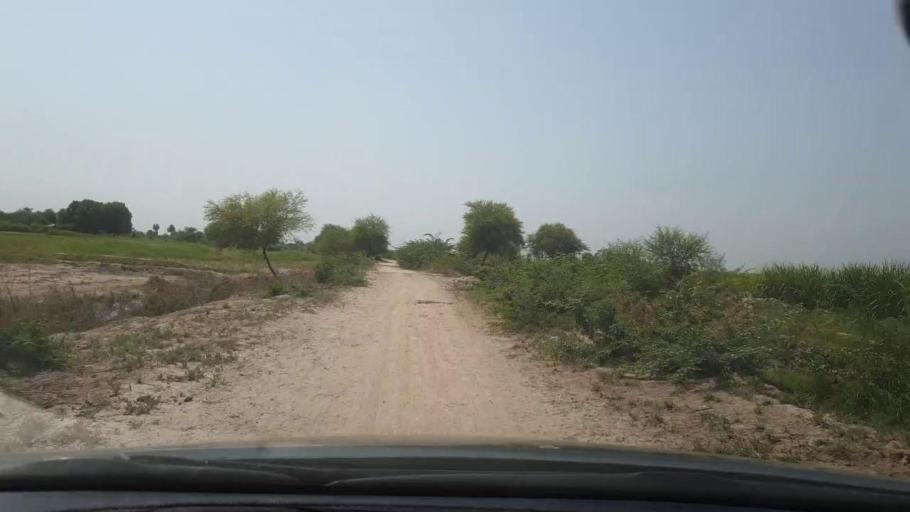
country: PK
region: Sindh
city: Tando Bago
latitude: 24.7725
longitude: 69.1763
